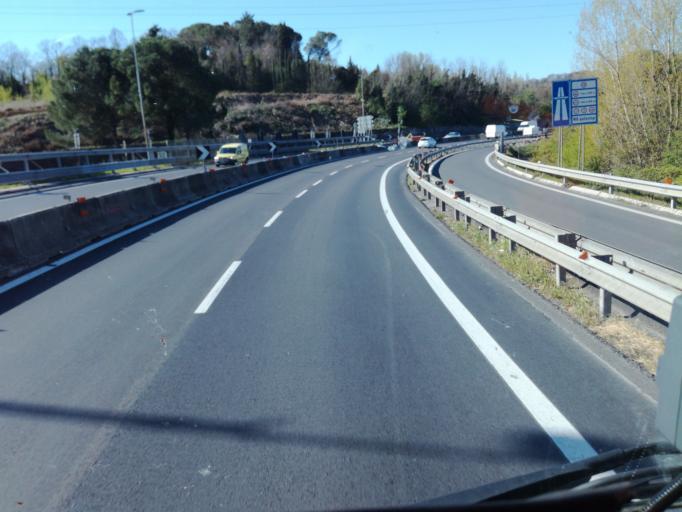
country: IT
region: Umbria
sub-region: Provincia di Perugia
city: Via Lippia
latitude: 43.0889
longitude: 12.4742
